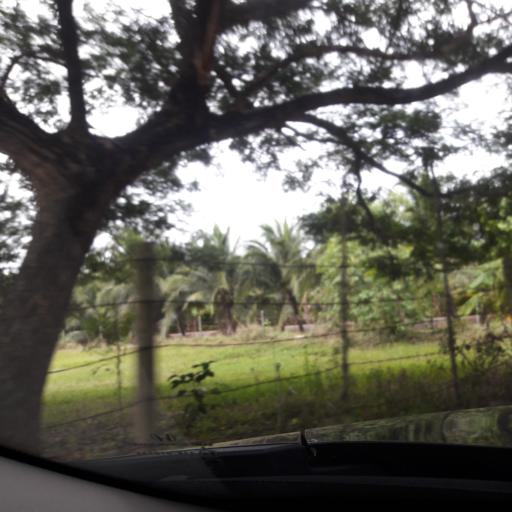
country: TH
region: Ratchaburi
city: Damnoen Saduak
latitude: 13.5819
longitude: 99.9475
